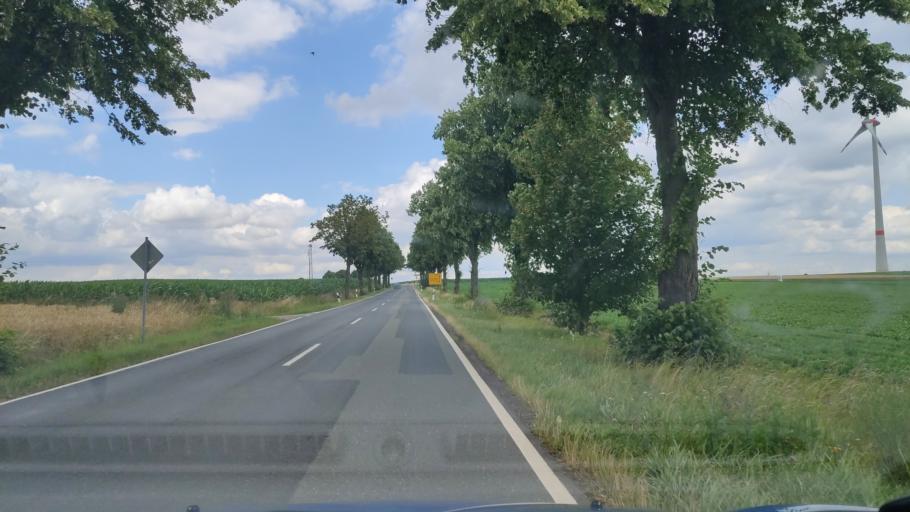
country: DE
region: Lower Saxony
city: Coppenbrugge
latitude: 52.1283
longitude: 9.4978
